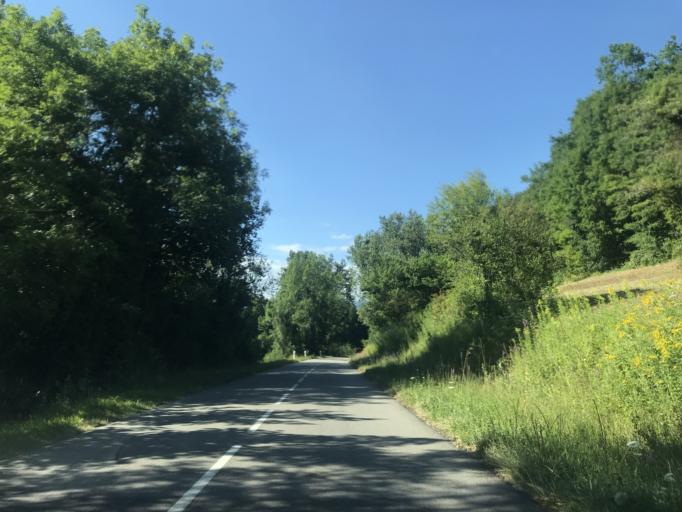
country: FR
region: Rhone-Alpes
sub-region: Departement de la Savoie
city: Yenne
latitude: 45.7557
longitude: 5.7862
